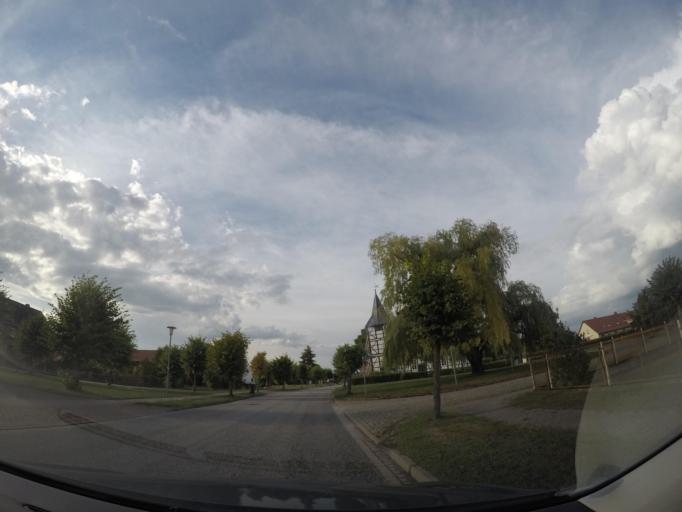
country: DE
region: Saxony-Anhalt
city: Kusey
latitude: 52.5633
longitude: 11.1349
